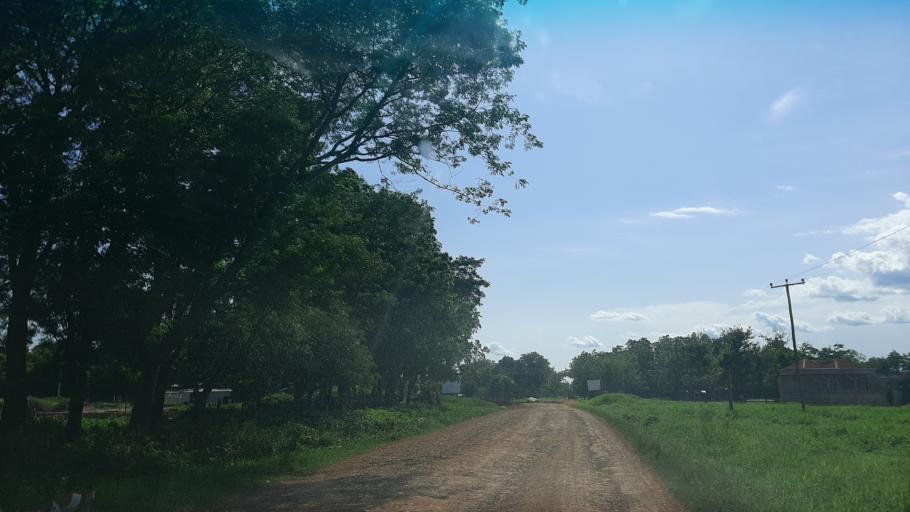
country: ET
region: Gambela
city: Gambela
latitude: 7.8973
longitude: 34.5454
